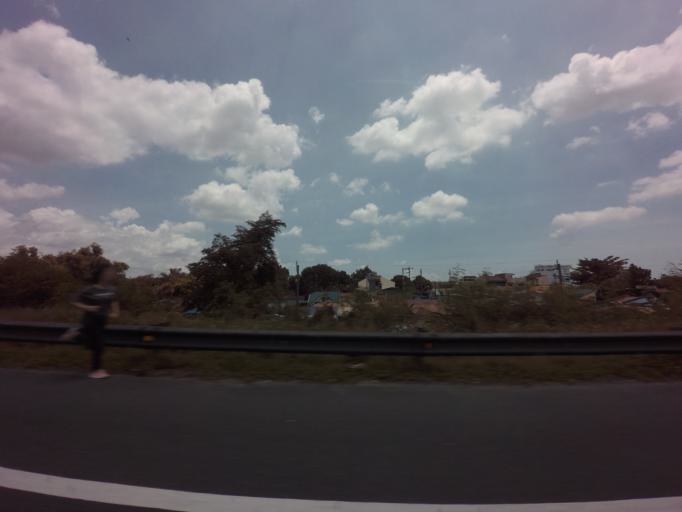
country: PH
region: Calabarzon
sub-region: Province of Laguna
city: San Pedro
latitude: 14.3972
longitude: 121.0387
